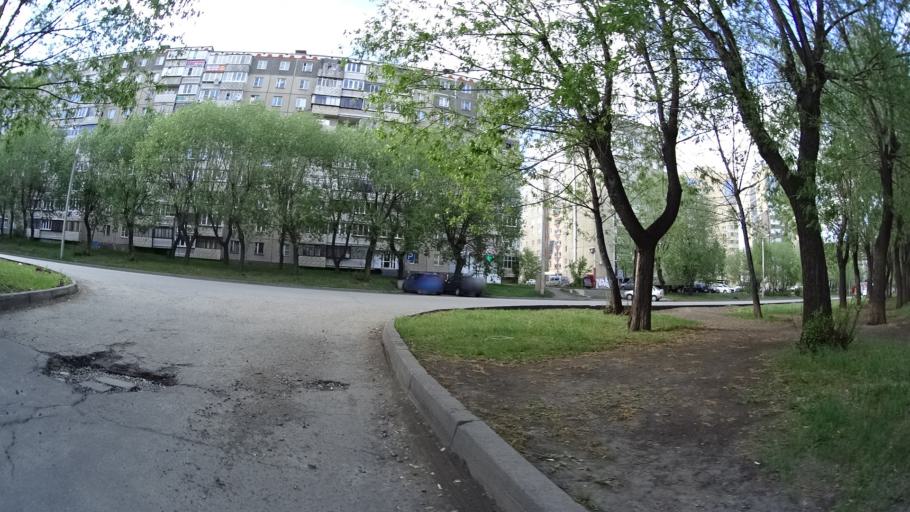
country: RU
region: Chelyabinsk
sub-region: Gorod Chelyabinsk
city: Chelyabinsk
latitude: 55.1763
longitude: 61.2965
